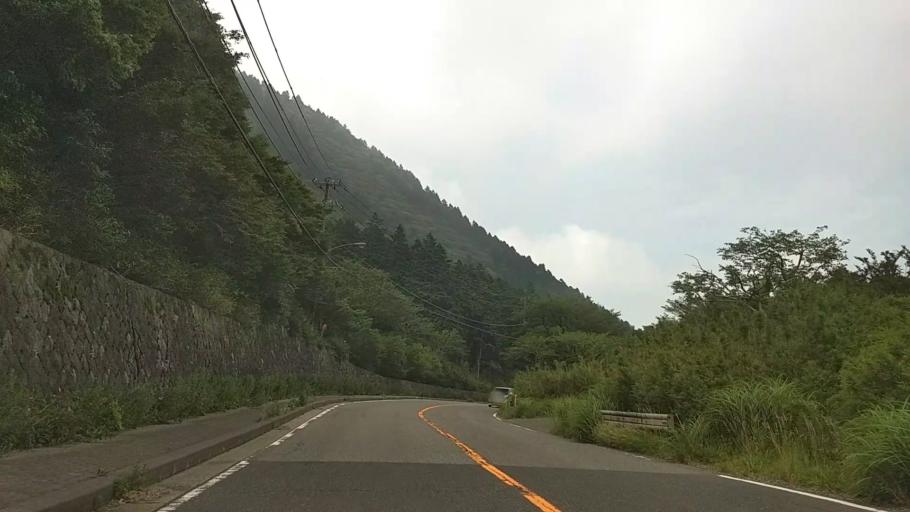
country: JP
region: Kanagawa
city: Hakone
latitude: 35.2169
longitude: 139.0381
